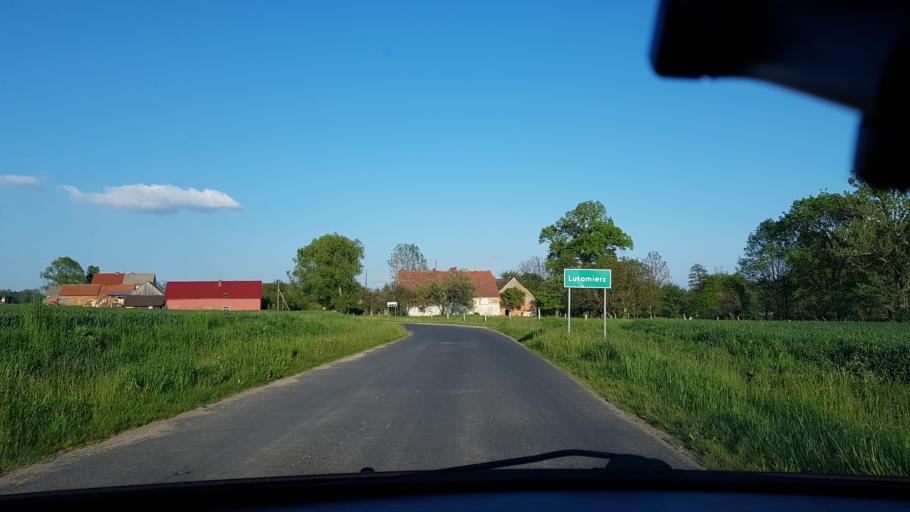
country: PL
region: Lower Silesian Voivodeship
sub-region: Powiat zabkowicki
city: Budzow
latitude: 50.6107
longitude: 16.7033
